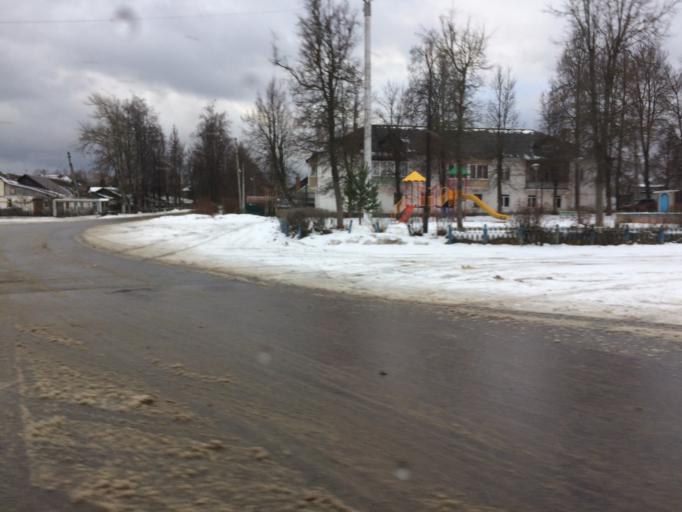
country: RU
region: Tula
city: Suvorov
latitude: 54.1183
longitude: 36.4955
